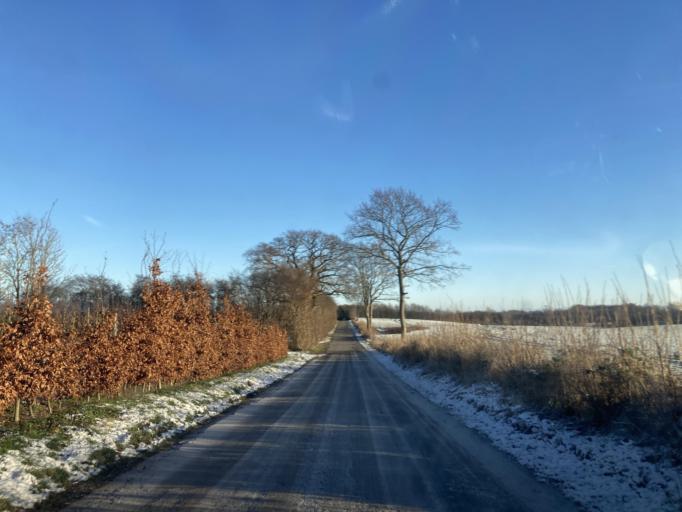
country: DK
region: South Denmark
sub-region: Svendborg Kommune
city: Thuro By
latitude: 55.1484
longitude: 10.7321
